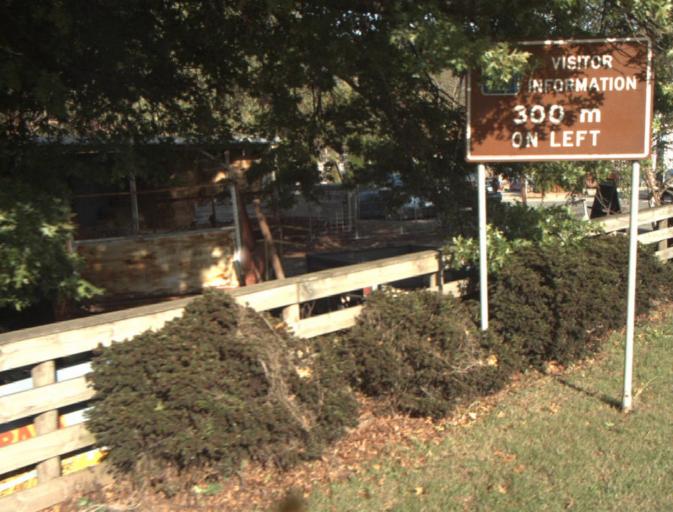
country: AU
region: Tasmania
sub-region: Launceston
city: Mayfield
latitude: -41.2484
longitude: 147.2178
